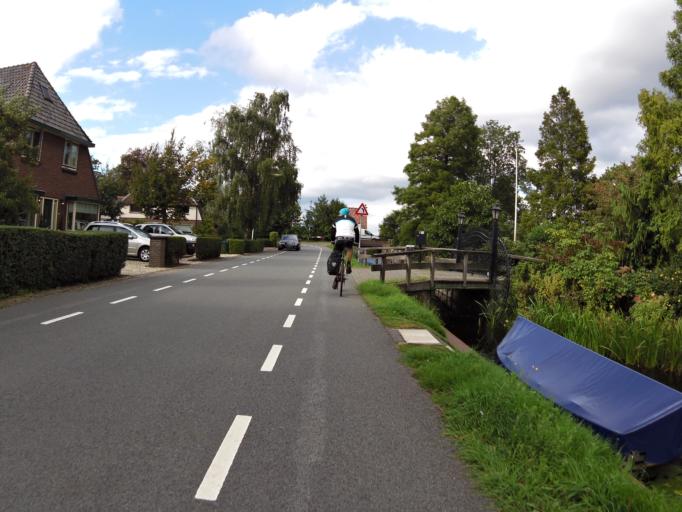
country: NL
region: North Holland
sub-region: Gemeente Wijdemeren
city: Oud-Loosdrecht
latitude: 52.1724
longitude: 5.0792
